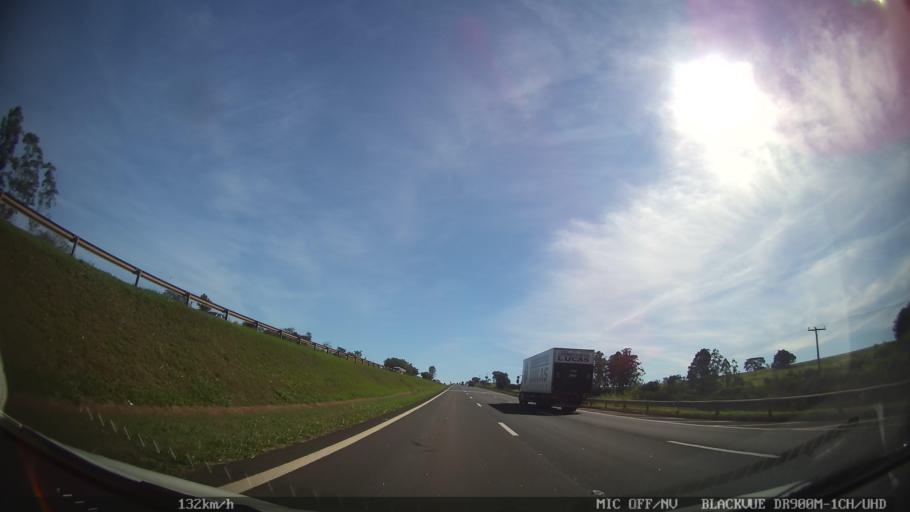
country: BR
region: Sao Paulo
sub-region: Pirassununga
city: Pirassununga
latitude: -22.0919
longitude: -47.4178
